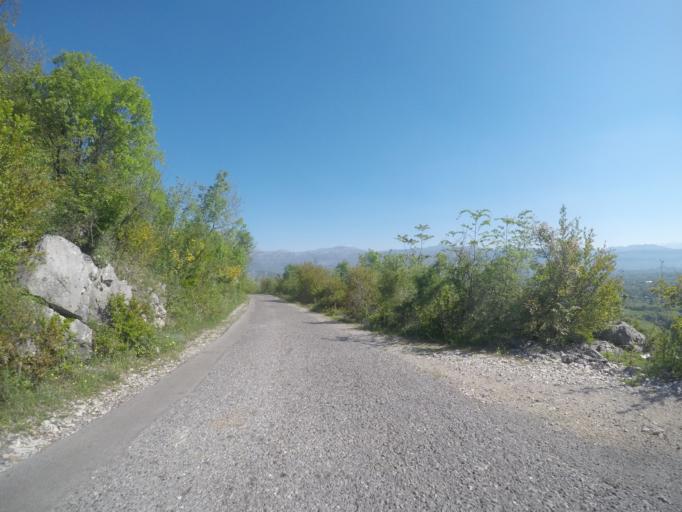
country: ME
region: Danilovgrad
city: Danilovgrad
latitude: 42.5155
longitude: 19.0982
